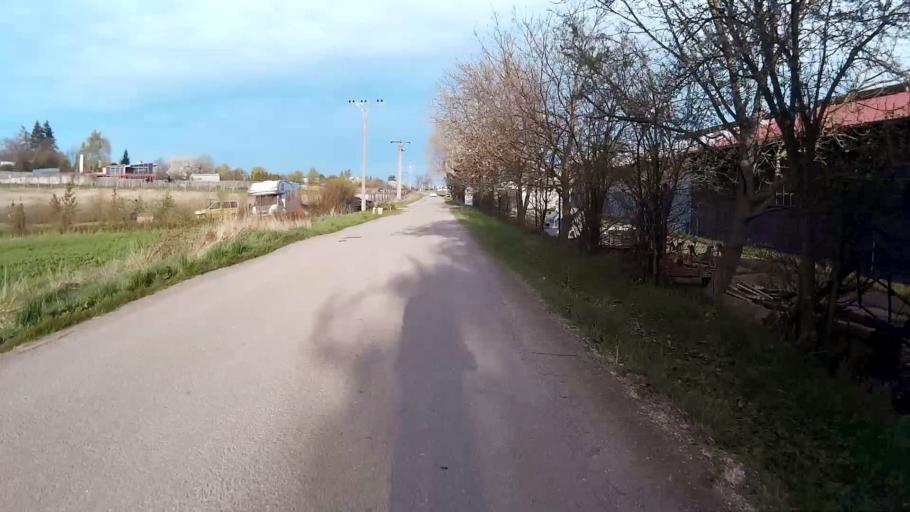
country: CZ
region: South Moravian
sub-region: Mesto Brno
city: Mokra Hora
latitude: 49.2421
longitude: 16.5588
